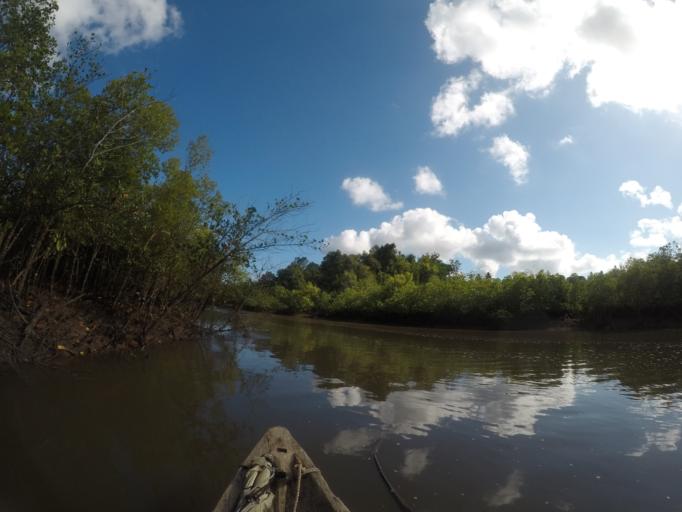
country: TZ
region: Pemba South
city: Mtambile
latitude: -5.3440
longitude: 39.6929
